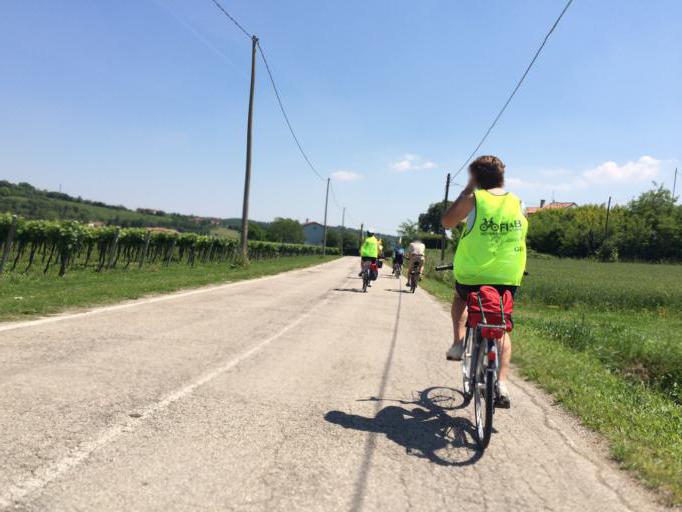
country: IT
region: Veneto
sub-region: Provincia di Vicenza
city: Villaga
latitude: 45.3998
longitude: 11.5413
